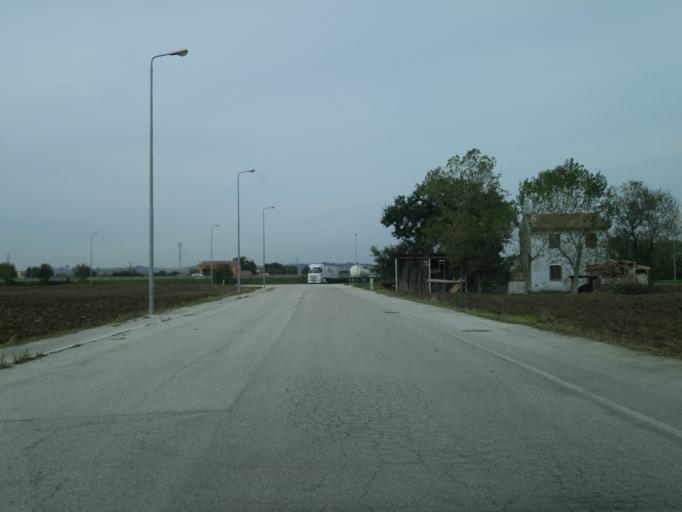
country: IT
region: The Marches
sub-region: Provincia di Pesaro e Urbino
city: Cuccurano
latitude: 43.7696
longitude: 12.9640
